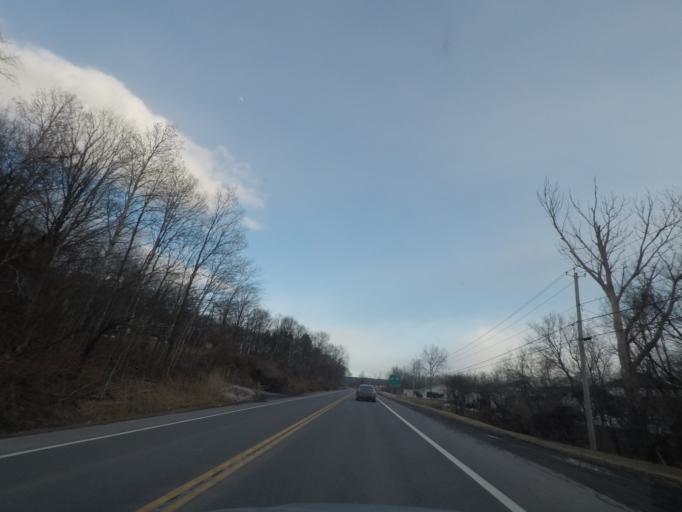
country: US
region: New York
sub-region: Herkimer County
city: Ilion
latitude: 43.0283
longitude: -75.0431
